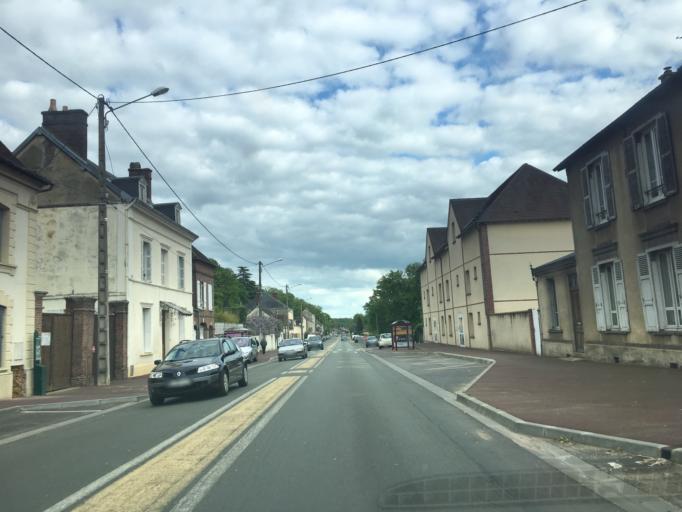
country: FR
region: Haute-Normandie
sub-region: Departement de l'Eure
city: La Madeleine-de-Nonancourt
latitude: 48.7701
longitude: 1.2012
